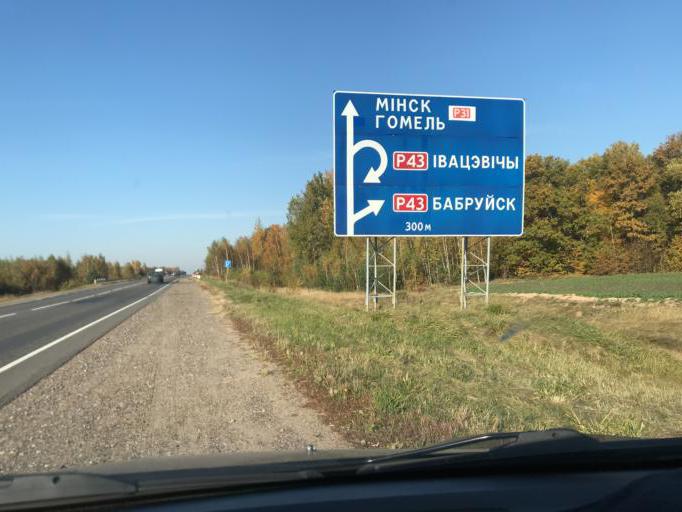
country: BY
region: Mogilev
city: Babruysk
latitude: 53.0999
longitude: 29.0582
